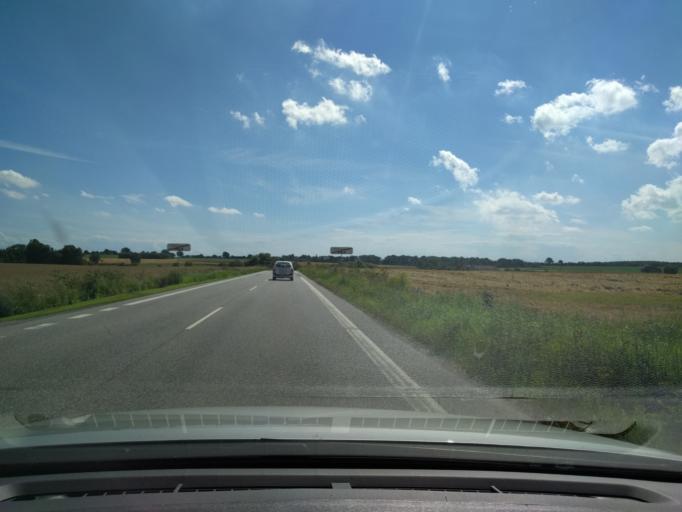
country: DK
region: Zealand
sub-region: Guldborgsund Kommune
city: Stubbekobing
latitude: 54.8599
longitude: 12.0180
